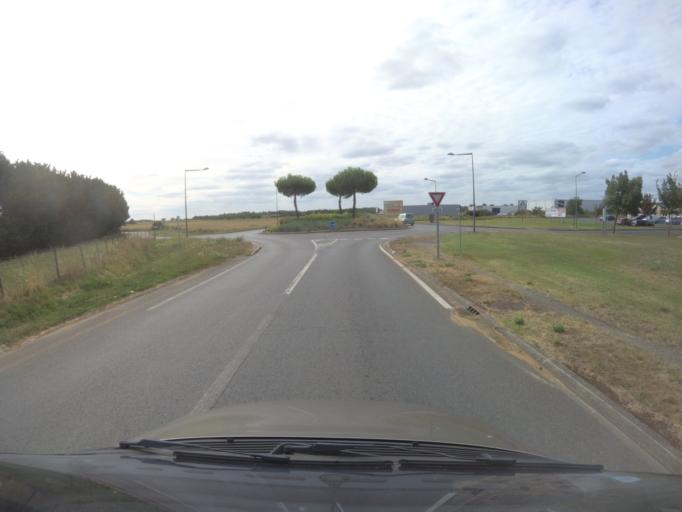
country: FR
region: Pays de la Loire
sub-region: Departement de Maine-et-Loire
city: Doue-la-Fontaine
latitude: 47.1883
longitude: -0.2881
